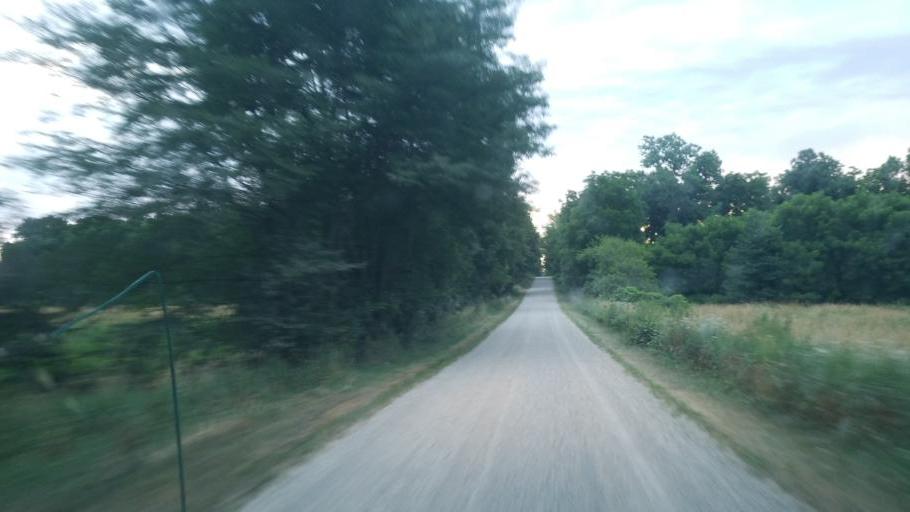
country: US
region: Ohio
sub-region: Defiance County
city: Hicksville
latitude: 41.3286
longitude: -84.8267
